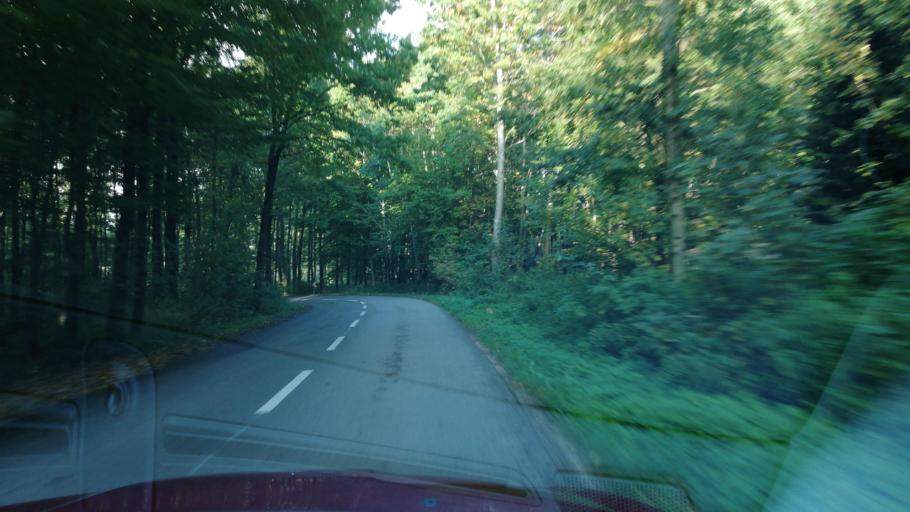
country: AT
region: Upper Austria
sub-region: Politischer Bezirk Grieskirchen
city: Bad Schallerbach
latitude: 48.2293
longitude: 13.9575
